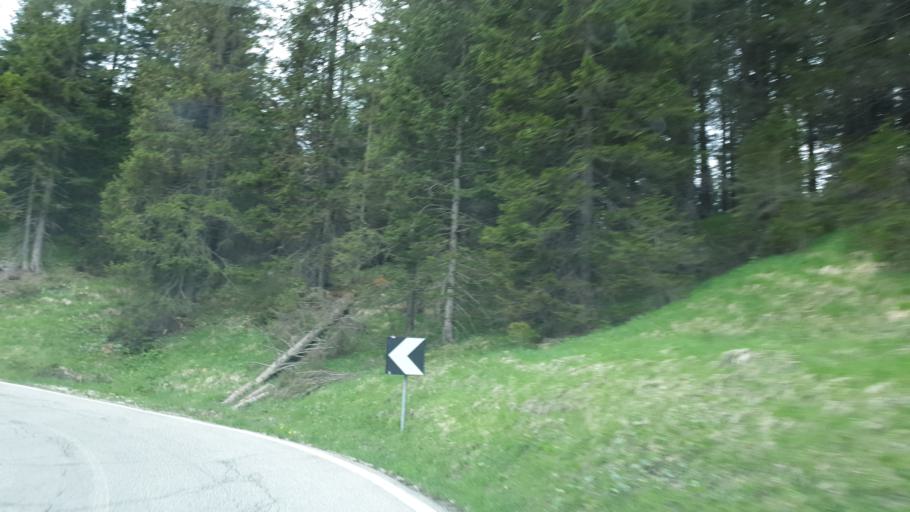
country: IT
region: Veneto
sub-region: Provincia di Belluno
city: San Vito
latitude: 46.5617
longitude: 12.2470
